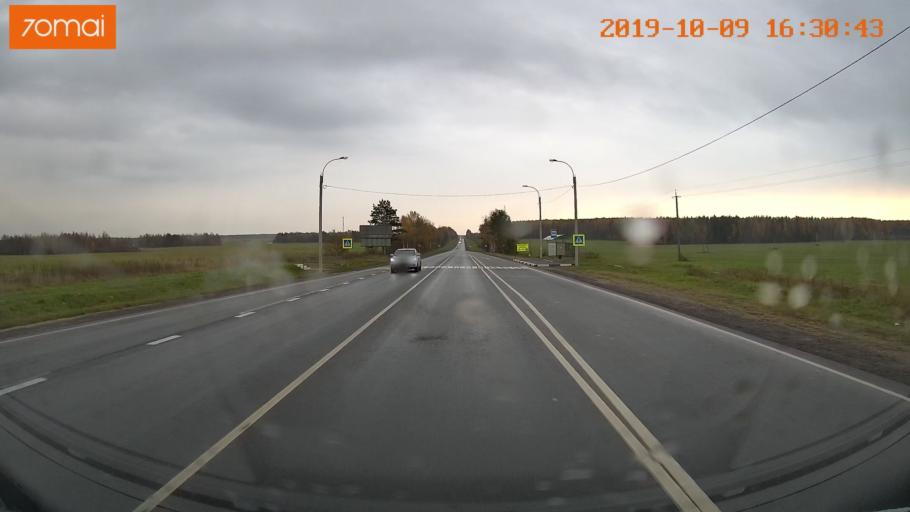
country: RU
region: Kostroma
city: Oktyabr'skiy
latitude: 57.6157
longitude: 40.9433
